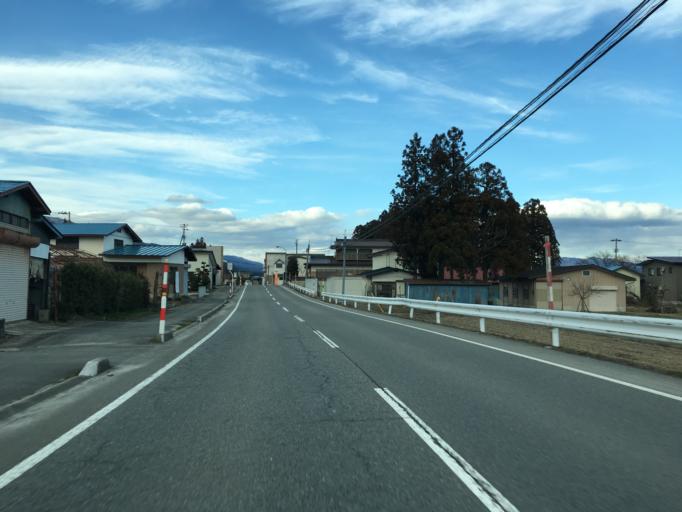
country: JP
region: Yamagata
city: Nagai
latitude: 38.1289
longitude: 140.0074
